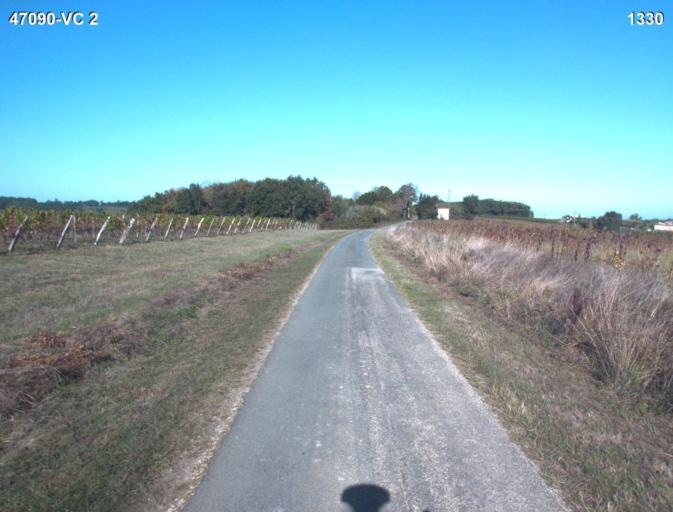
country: FR
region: Aquitaine
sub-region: Departement du Lot-et-Garonne
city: Vianne
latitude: 44.1804
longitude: 0.3691
